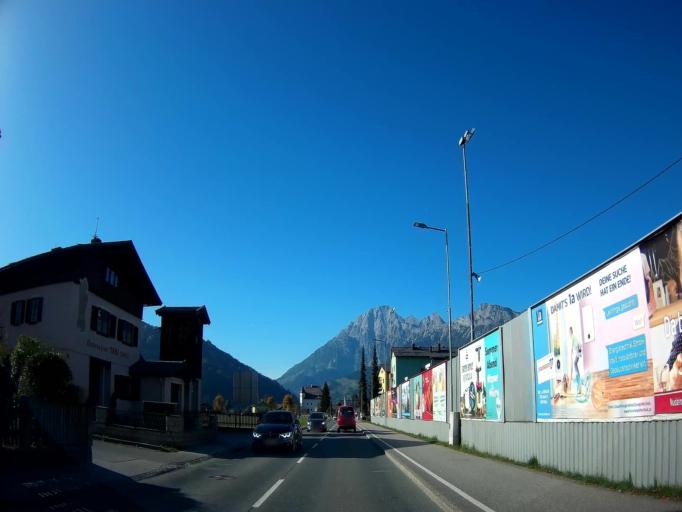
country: AT
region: Salzburg
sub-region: Politischer Bezirk Zell am See
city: Saalfelden am Steinernen Meer
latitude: 47.4301
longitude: 12.8399
